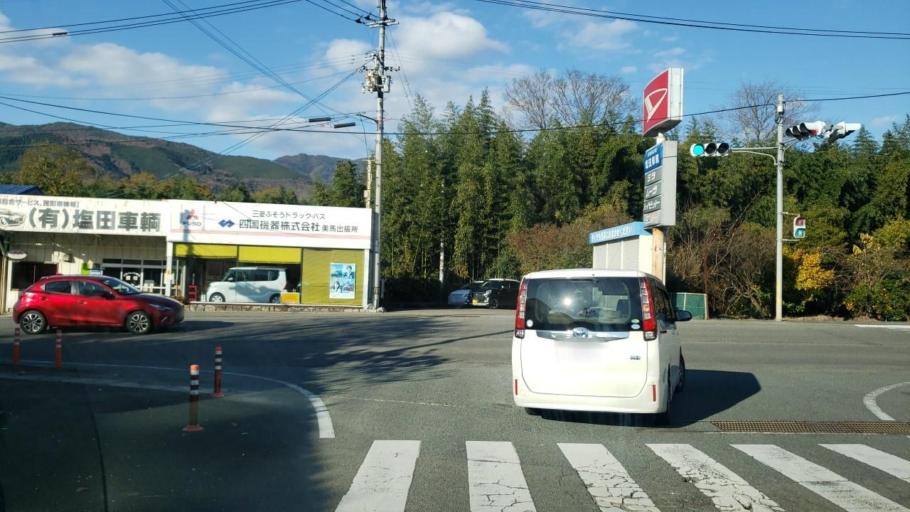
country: JP
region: Tokushima
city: Wakimachi
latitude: 34.0418
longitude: 134.0285
